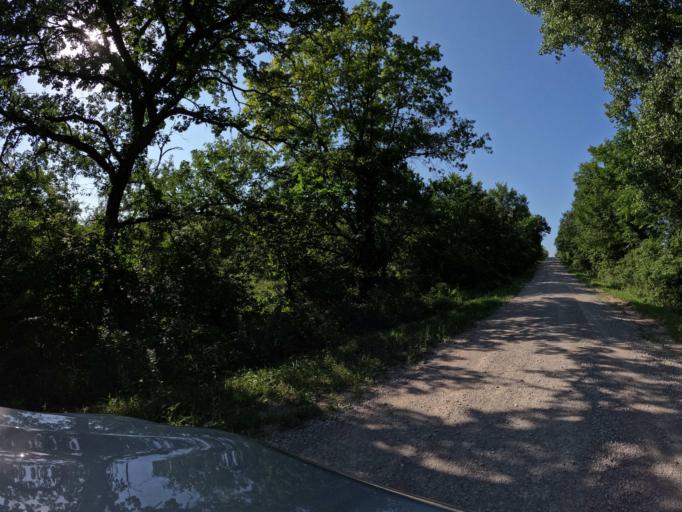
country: US
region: Iowa
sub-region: Appanoose County
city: Centerville
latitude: 40.7335
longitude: -93.0207
